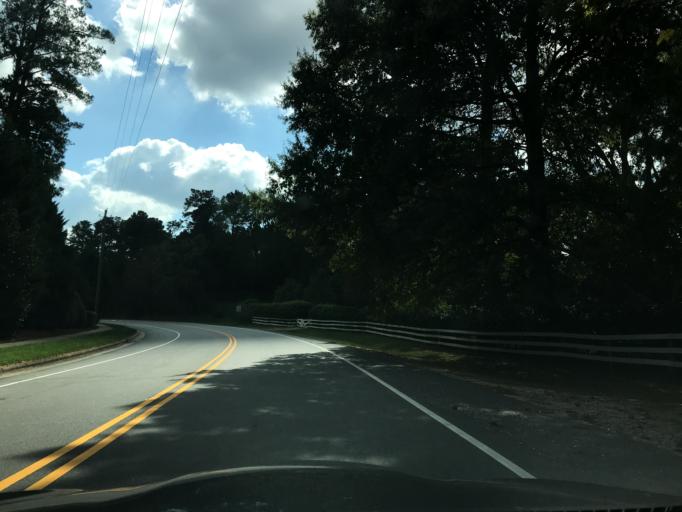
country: US
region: North Carolina
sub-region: Wake County
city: Wake Forest
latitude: 35.9396
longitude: -78.5336
